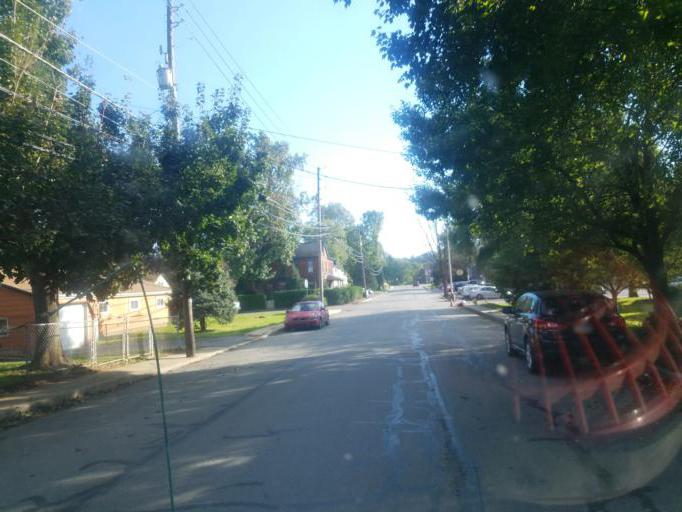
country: US
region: Pennsylvania
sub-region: Lancaster County
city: Marietta
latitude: 40.0574
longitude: -76.5678
